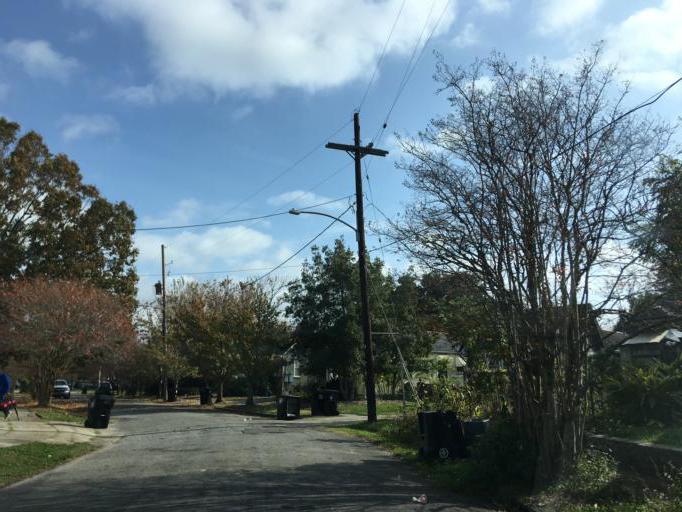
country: US
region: Louisiana
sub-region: Orleans Parish
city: New Orleans
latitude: 29.9969
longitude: -90.0588
